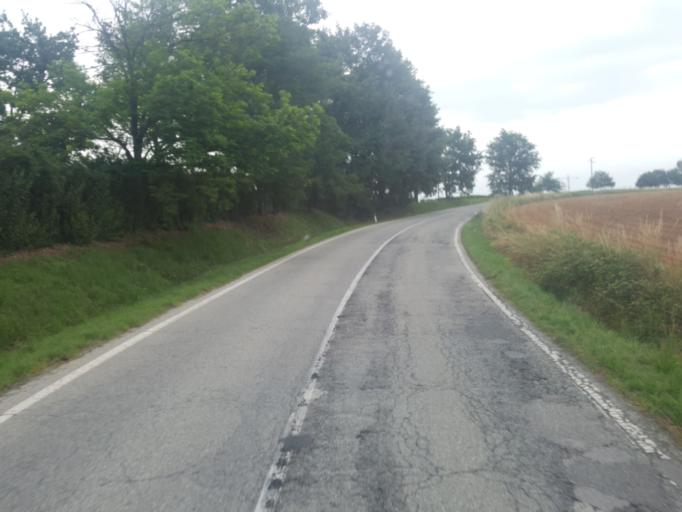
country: IT
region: Piedmont
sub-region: Provincia di Cuneo
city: Ceresole Alba
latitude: 44.8567
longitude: 7.8194
